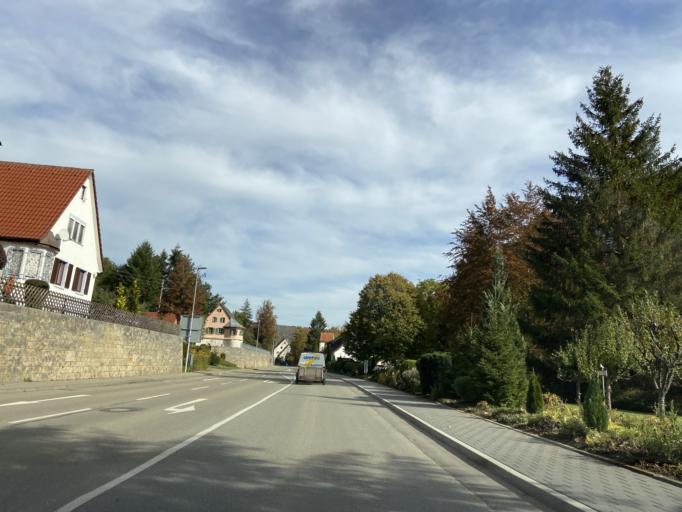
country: DE
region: Baden-Wuerttemberg
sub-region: Tuebingen Region
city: Schwenningen
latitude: 48.0825
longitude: 9.0352
